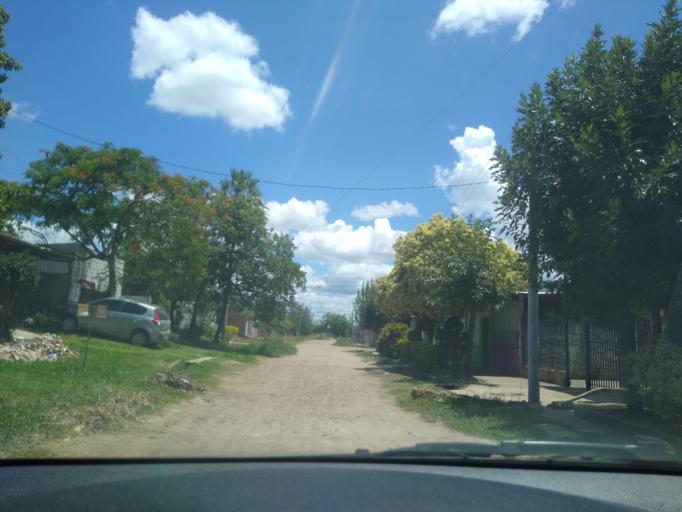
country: AR
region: Chaco
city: Barranqueras
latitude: -27.4759
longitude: -58.9353
